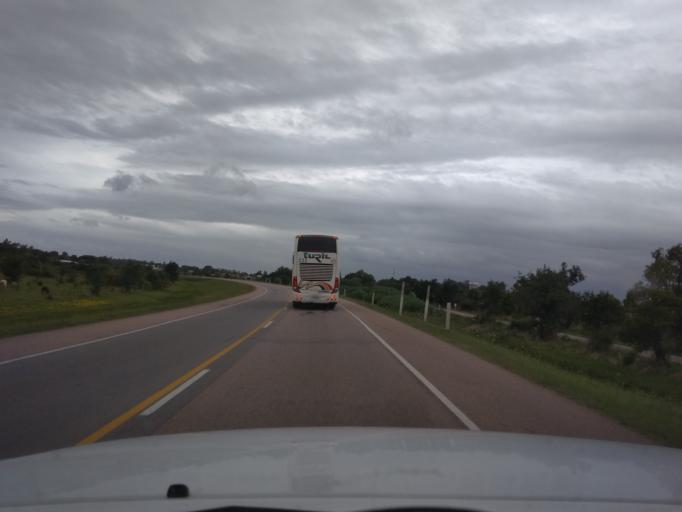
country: UY
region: Canelones
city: Canelones
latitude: -34.5054
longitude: -56.2814
